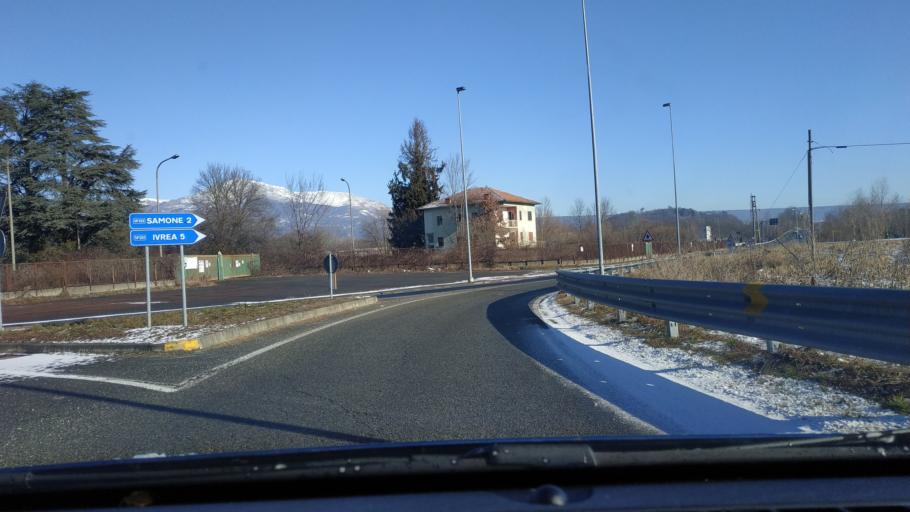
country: IT
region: Piedmont
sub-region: Provincia di Torino
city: Loranze
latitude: 45.4423
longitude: 7.8218
